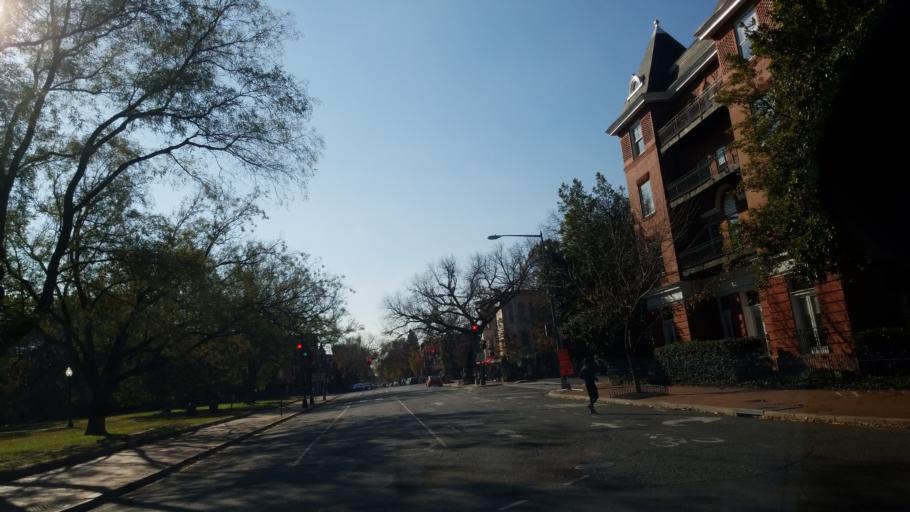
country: US
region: Washington, D.C.
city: Washington, D.C.
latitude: 38.8904
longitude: -76.9916
